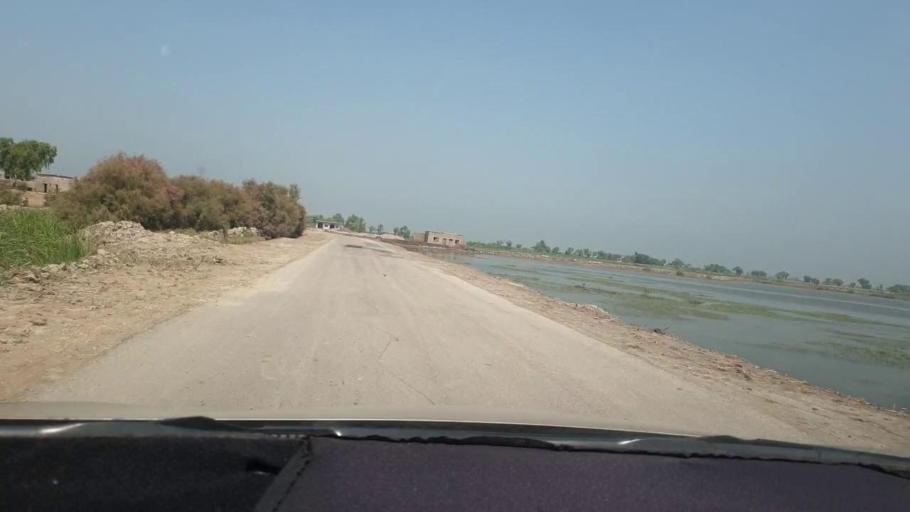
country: PK
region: Sindh
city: Miro Khan
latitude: 27.8155
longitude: 68.0275
